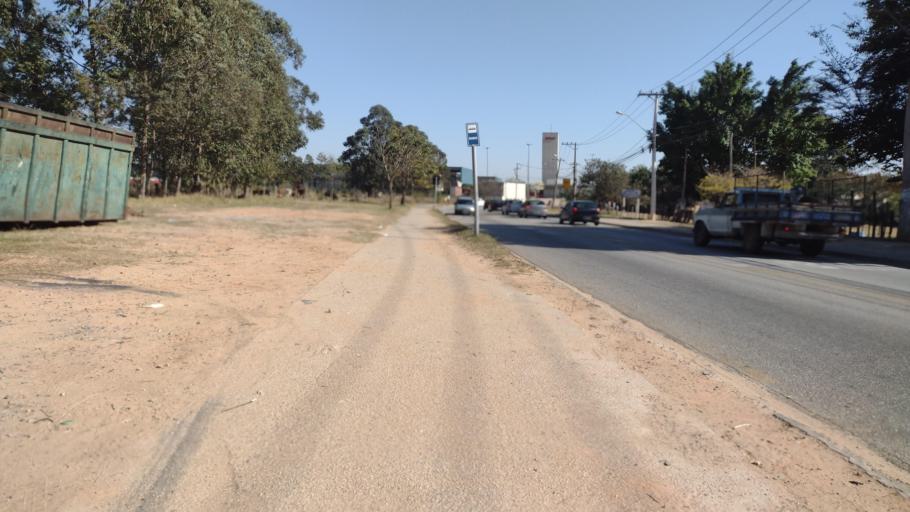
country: BR
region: Sao Paulo
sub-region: Sorocaba
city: Sorocaba
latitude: -23.4306
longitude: -47.4819
